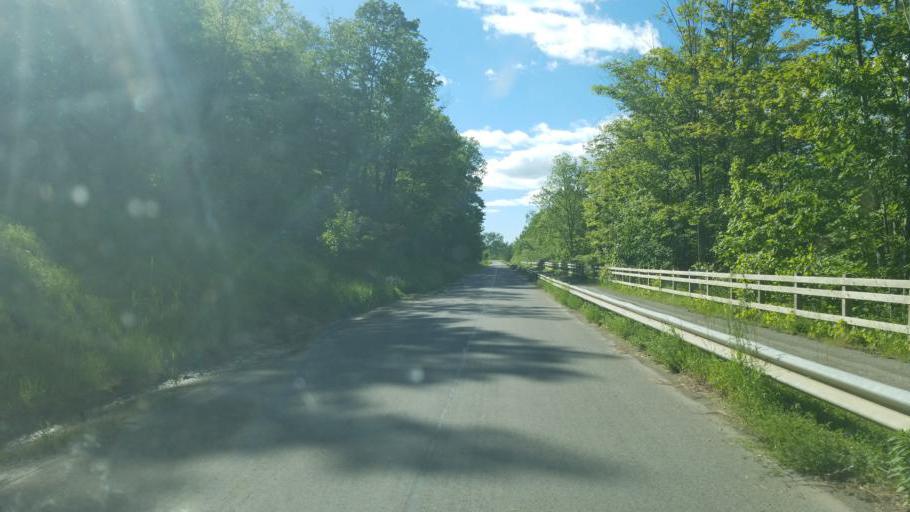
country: US
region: New York
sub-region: Montgomery County
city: Saint Johnsville
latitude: 42.9939
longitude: -74.7344
